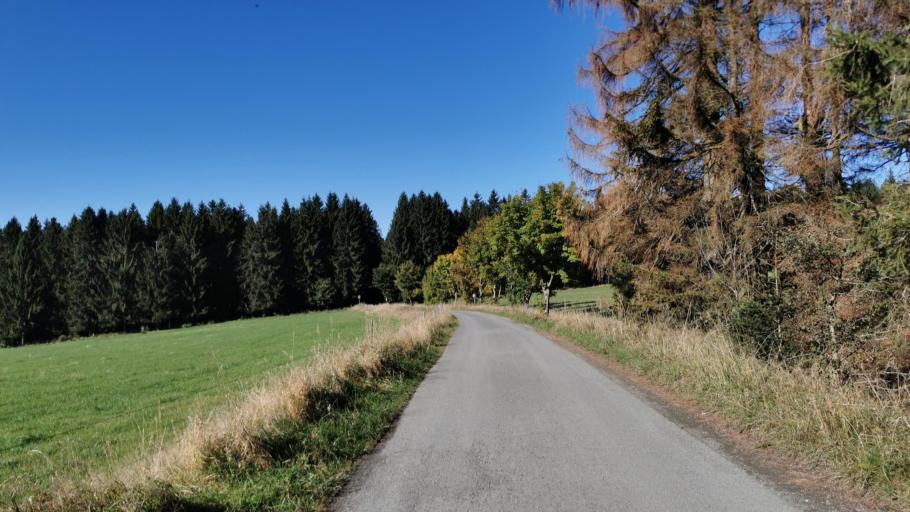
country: DE
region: Bavaria
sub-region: Upper Franconia
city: Tettau
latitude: 50.4856
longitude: 11.2824
